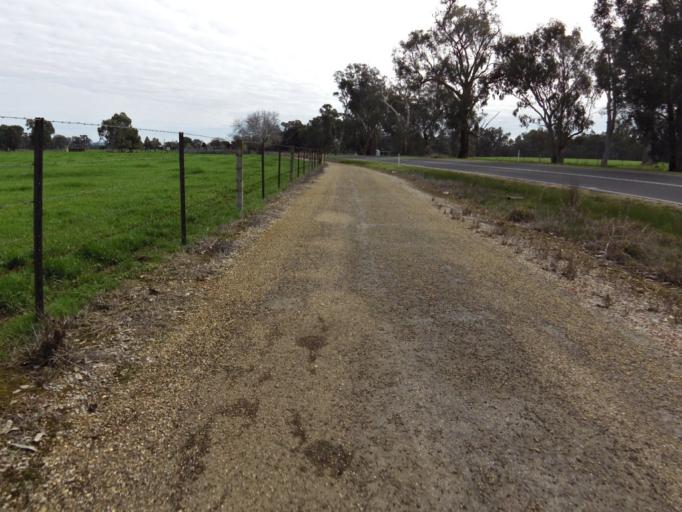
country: AU
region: Victoria
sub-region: Wangaratta
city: Wangaratta
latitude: -36.4124
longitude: 146.3532
